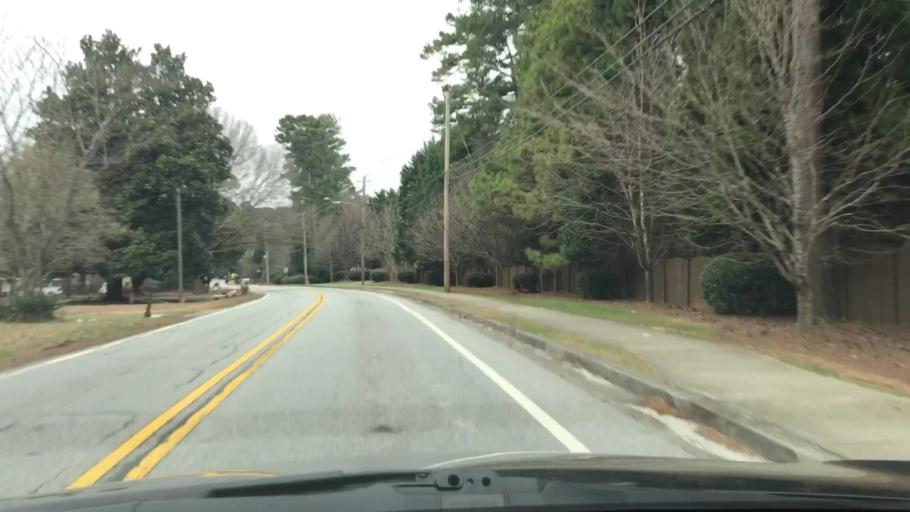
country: US
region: Georgia
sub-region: DeKalb County
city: Doraville
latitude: 33.9298
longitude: -84.2839
